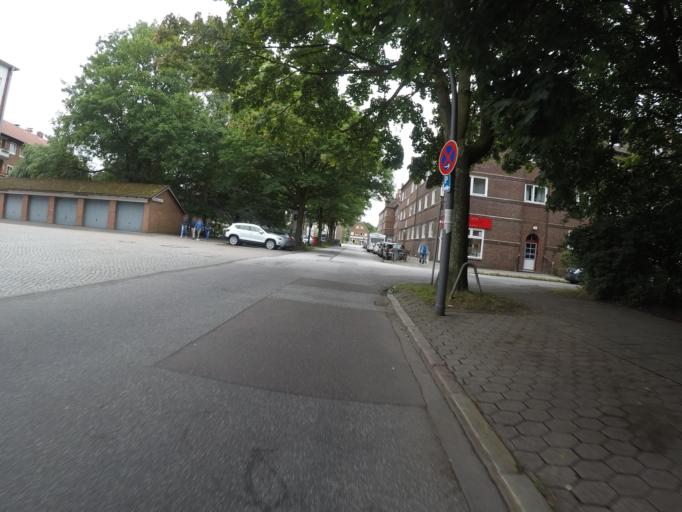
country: DE
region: Hamburg
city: Altona
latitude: 53.5346
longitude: 9.8790
